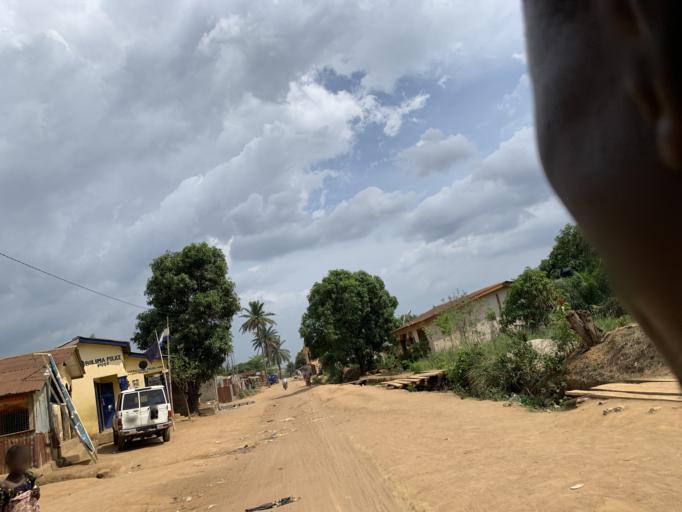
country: SL
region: Western Area
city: Waterloo
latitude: 8.3396
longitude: -13.0528
